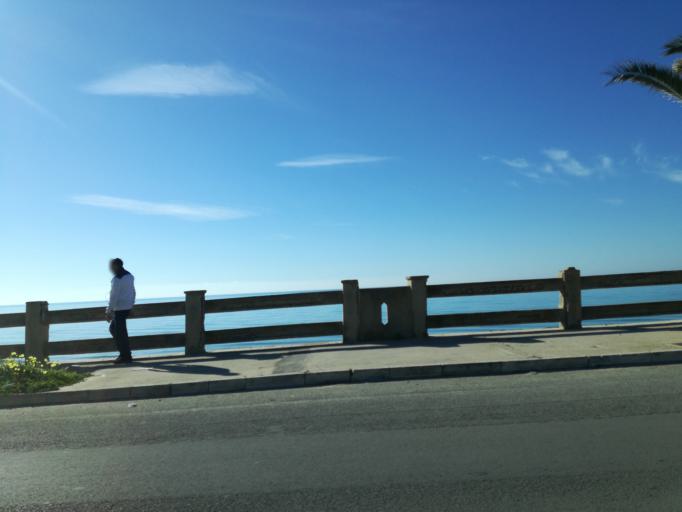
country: IT
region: Sicily
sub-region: Provincia di Caltanissetta
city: Gela
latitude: 37.0726
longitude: 14.2186
